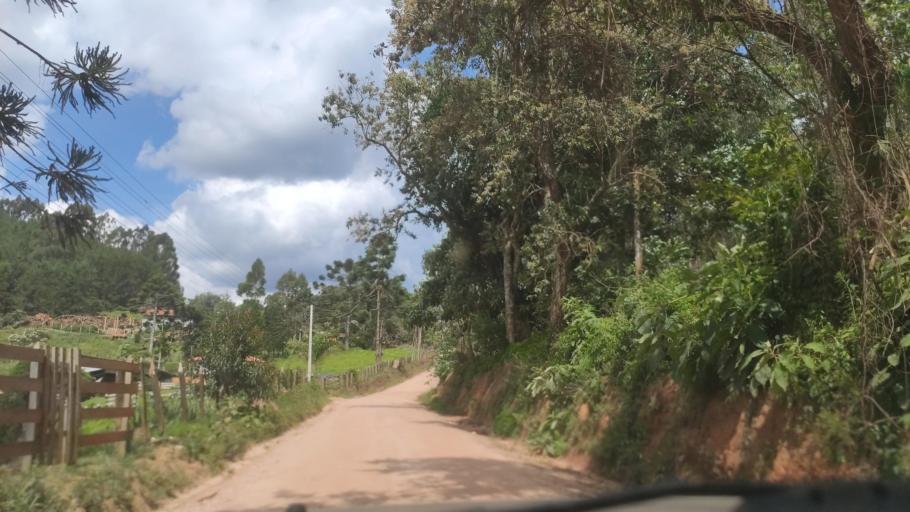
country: BR
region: Minas Gerais
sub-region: Camanducaia
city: Camanducaia
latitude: -22.7713
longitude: -46.0074
